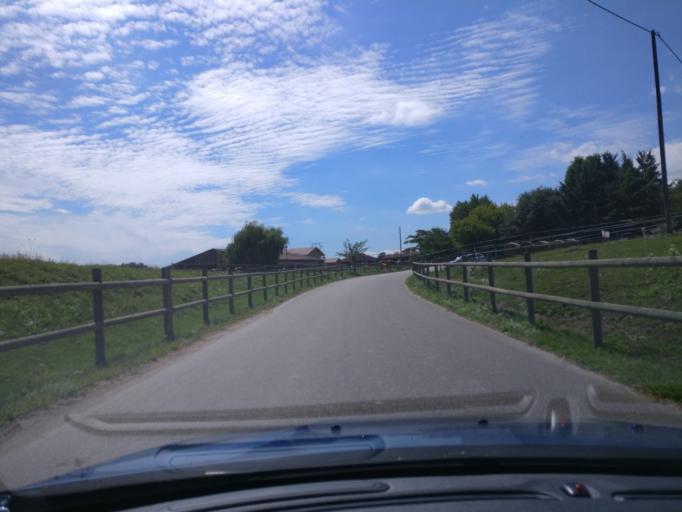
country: FR
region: Rhone-Alpes
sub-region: Departement de l'Ain
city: Sergy
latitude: 46.2327
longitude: 6.0042
